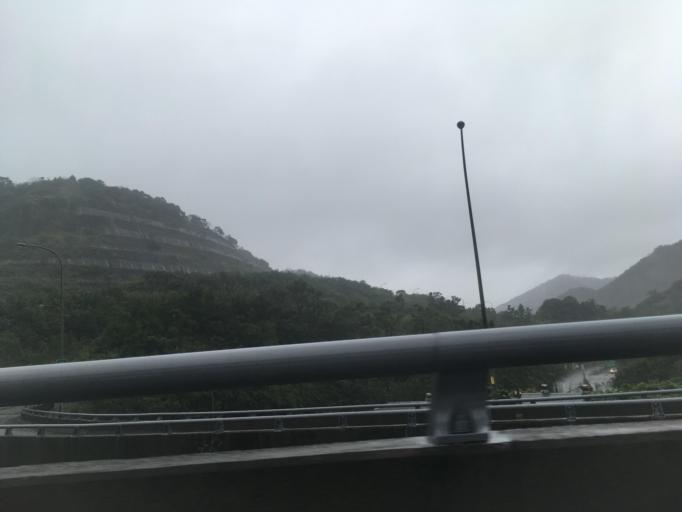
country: TW
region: Taiwan
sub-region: Keelung
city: Keelung
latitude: 25.1147
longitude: 121.6907
